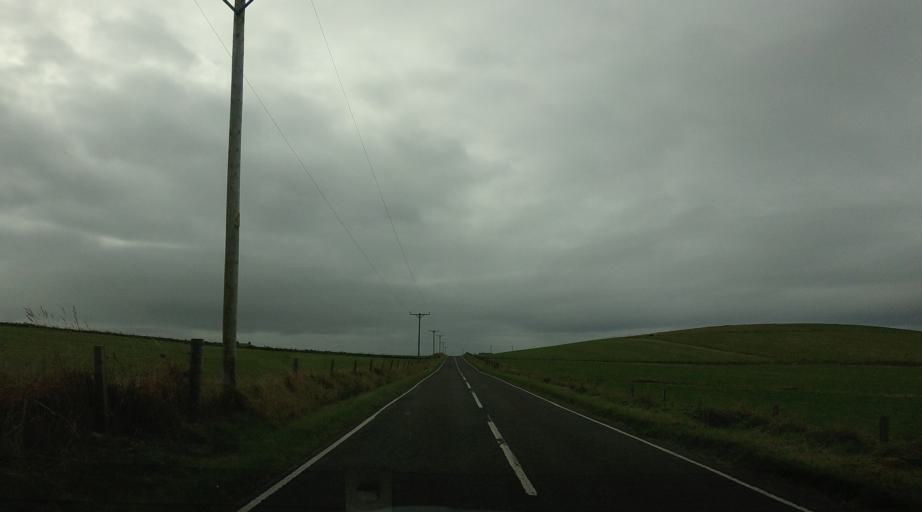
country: GB
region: Scotland
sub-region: Orkney Islands
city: Orkney
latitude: 58.7989
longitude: -2.9637
